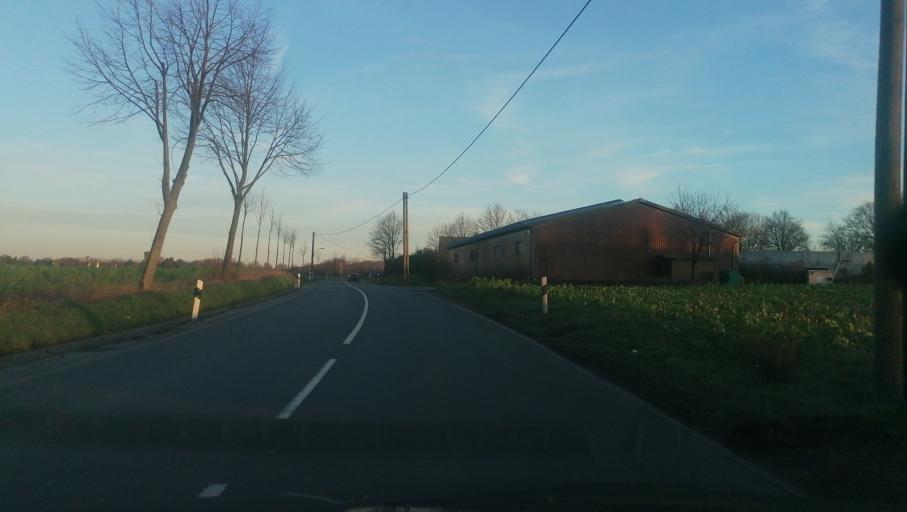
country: DE
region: North Rhine-Westphalia
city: Bergkamen
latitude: 51.5980
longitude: 7.6153
